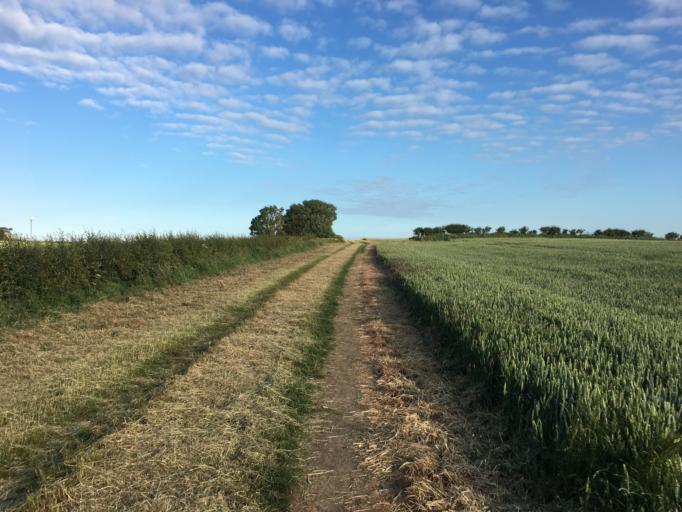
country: GB
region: England
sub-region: Northumberland
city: Bamburgh
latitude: 55.6007
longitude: -1.6984
